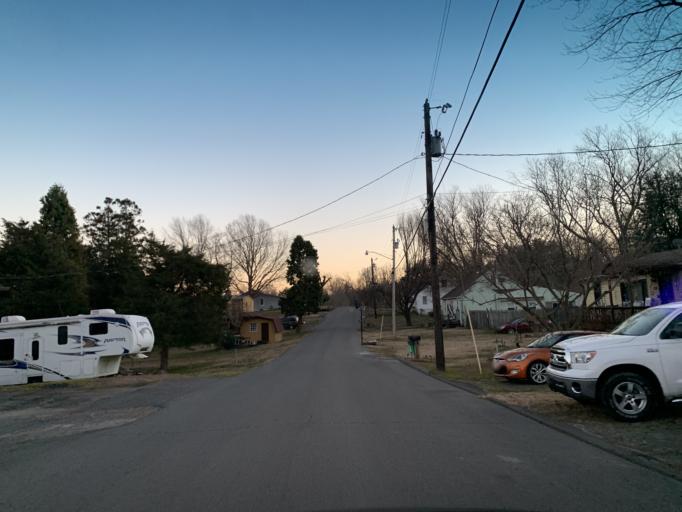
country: US
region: Maryland
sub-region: Calvert County
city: Prince Frederick
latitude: 38.5596
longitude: -76.5175
